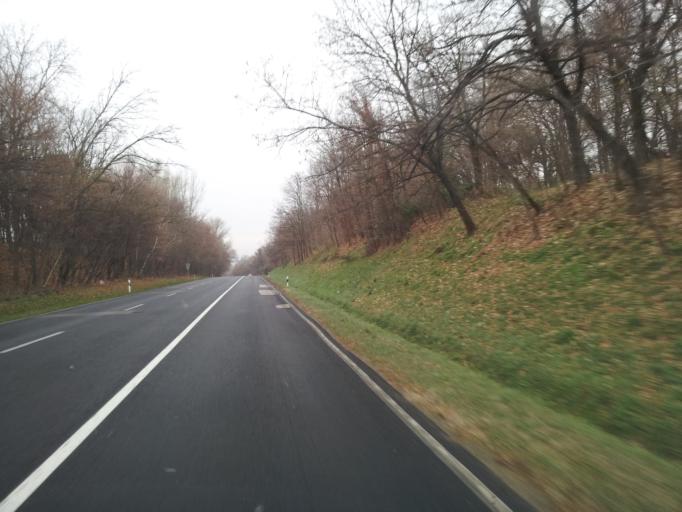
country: HU
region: Veszprem
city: Ajka
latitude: 47.1420
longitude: 17.5699
